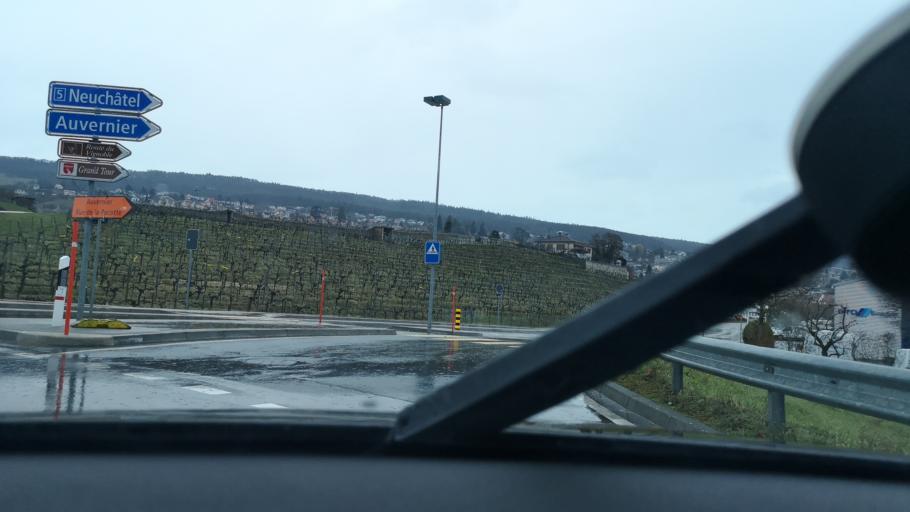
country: CH
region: Neuchatel
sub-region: Boudry District
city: Auvernier
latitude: 46.9712
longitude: 6.8707
